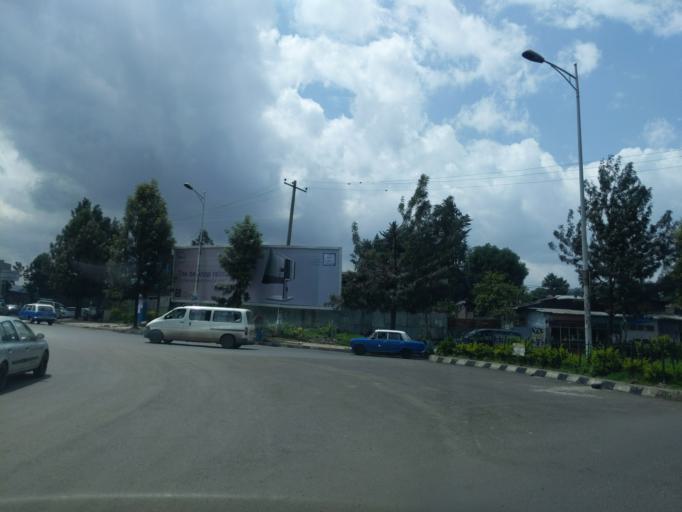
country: ET
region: Adis Abeba
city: Addis Ababa
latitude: 9.0228
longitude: 38.7772
